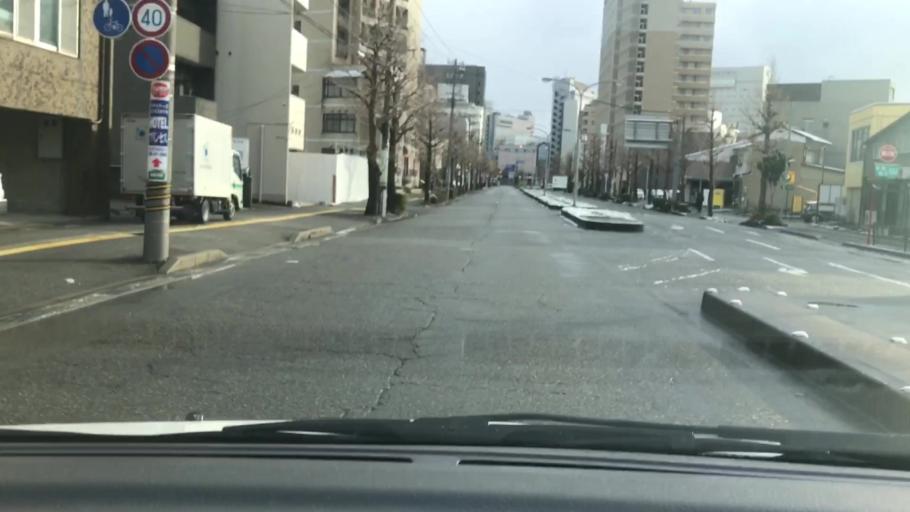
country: JP
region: Toyama
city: Toyama-shi
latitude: 36.7003
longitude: 137.2071
